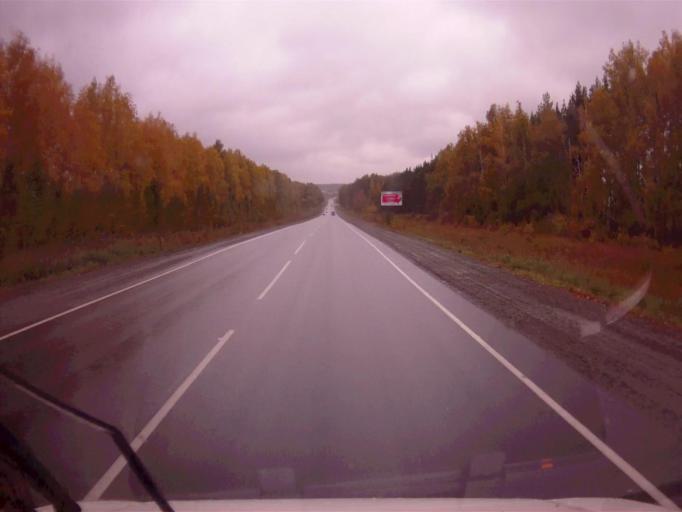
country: RU
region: Chelyabinsk
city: Roshchino
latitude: 55.3624
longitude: 61.2127
